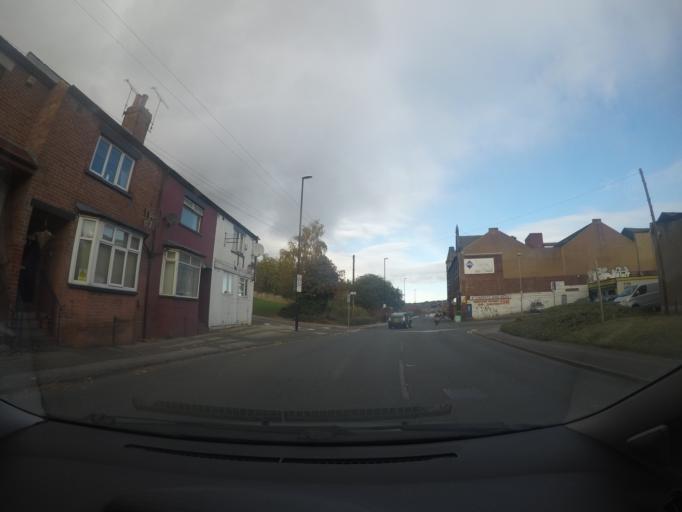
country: GB
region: England
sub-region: City and Borough of Leeds
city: Leeds
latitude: 53.8003
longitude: -1.5833
